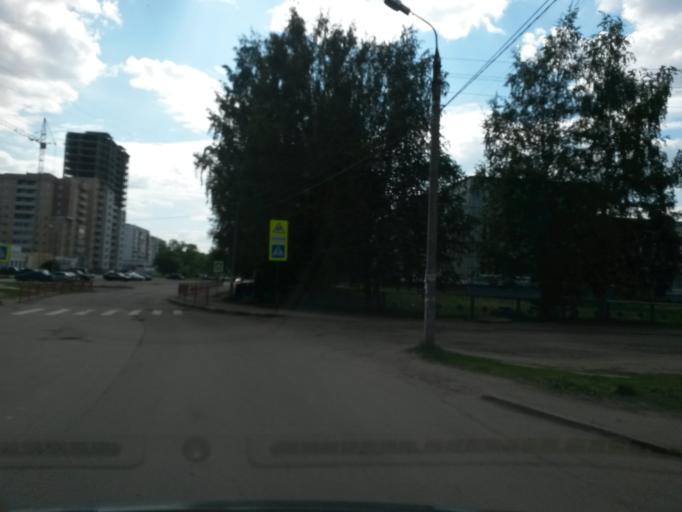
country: RU
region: Jaroslavl
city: Yaroslavl
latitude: 57.6458
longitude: 39.9508
